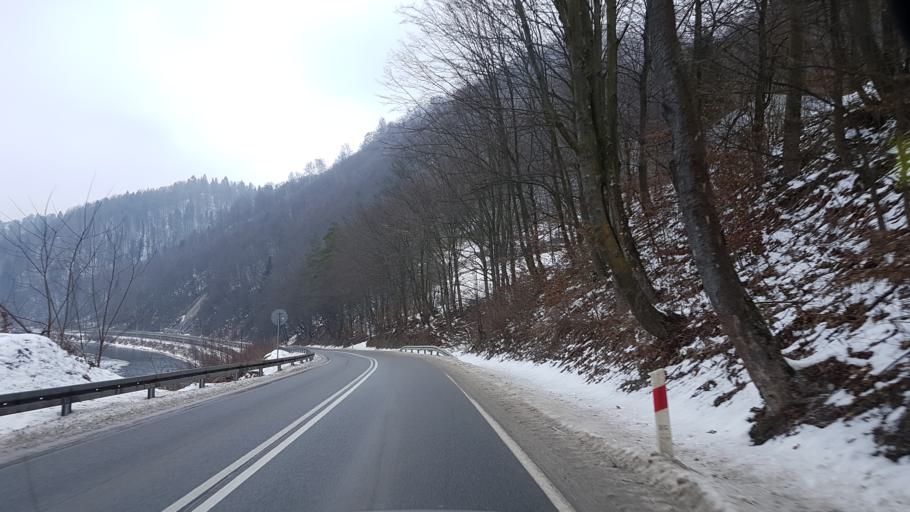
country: PL
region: Lesser Poland Voivodeship
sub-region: Powiat nowosadecki
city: Piwniczna-Zdroj
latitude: 49.4116
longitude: 20.7471
